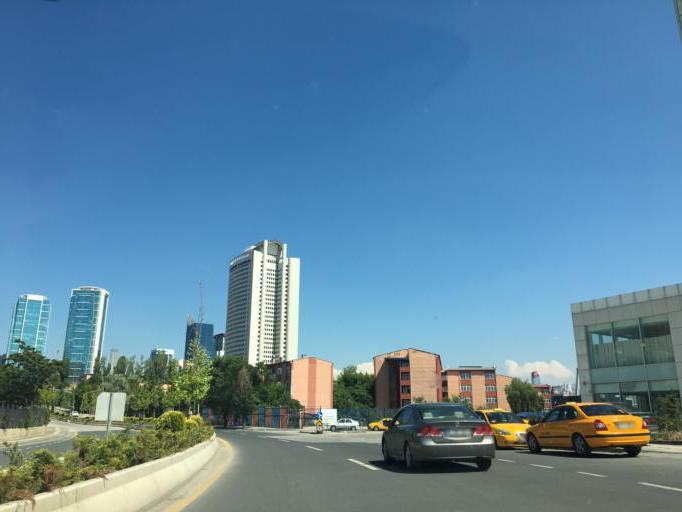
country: TR
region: Ankara
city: Ankara
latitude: 39.9127
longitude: 32.7881
